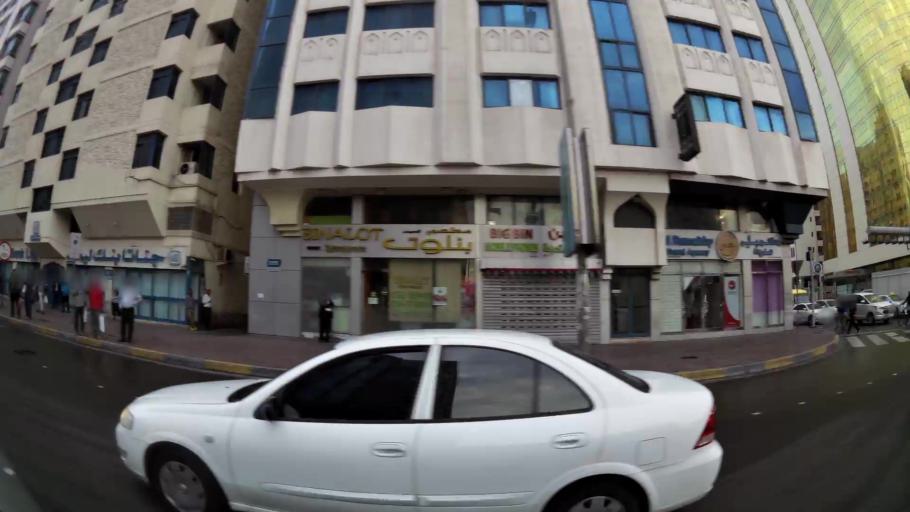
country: AE
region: Abu Dhabi
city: Abu Dhabi
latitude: 24.4870
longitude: 54.3645
